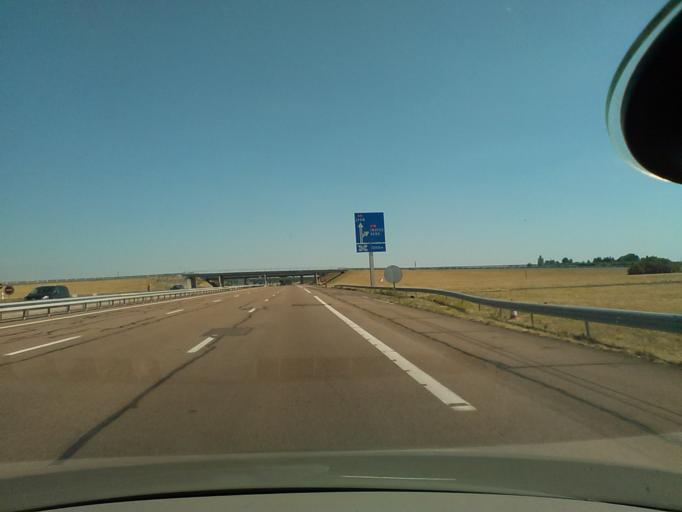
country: FR
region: Centre
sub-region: Departement du Loiret
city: Courtenay
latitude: 48.0579
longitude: 3.0937
